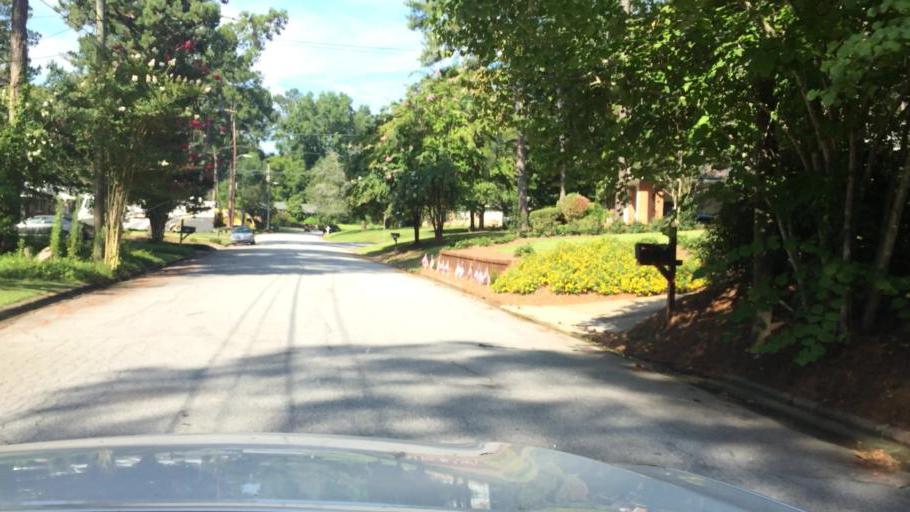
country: US
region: Georgia
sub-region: Columbia County
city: Martinez
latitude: 33.4933
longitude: -82.0395
